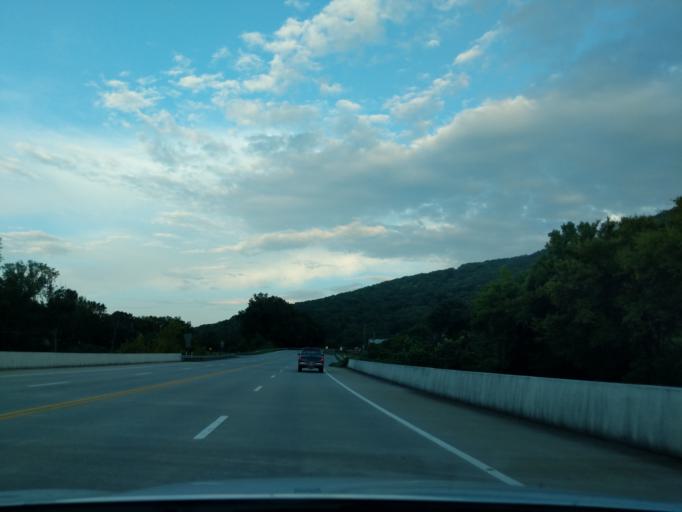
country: US
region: Tennessee
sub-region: Hamilton County
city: Lookout Mountain
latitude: 35.0212
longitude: -85.3569
